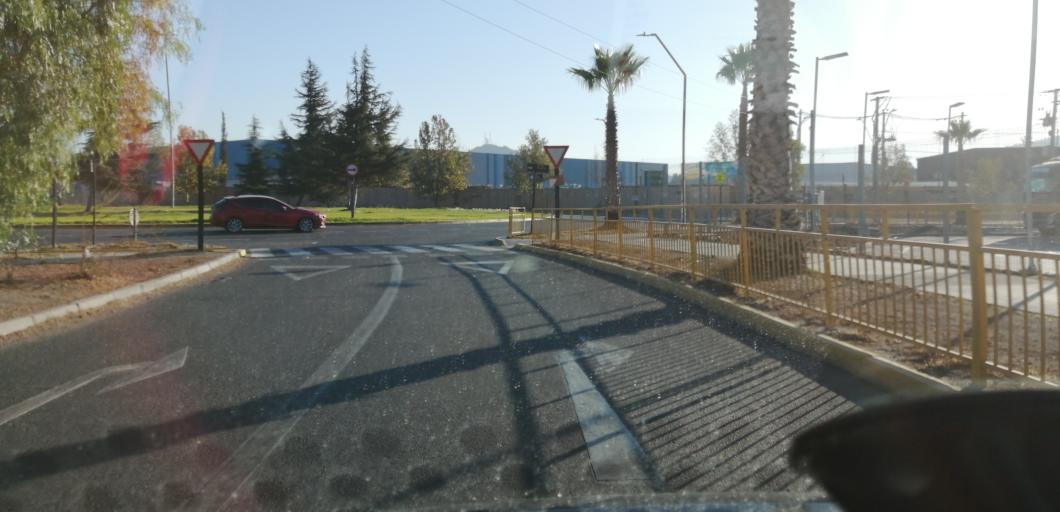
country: CL
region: Santiago Metropolitan
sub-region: Provincia de Santiago
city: Lo Prado
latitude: -33.4476
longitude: -70.8451
